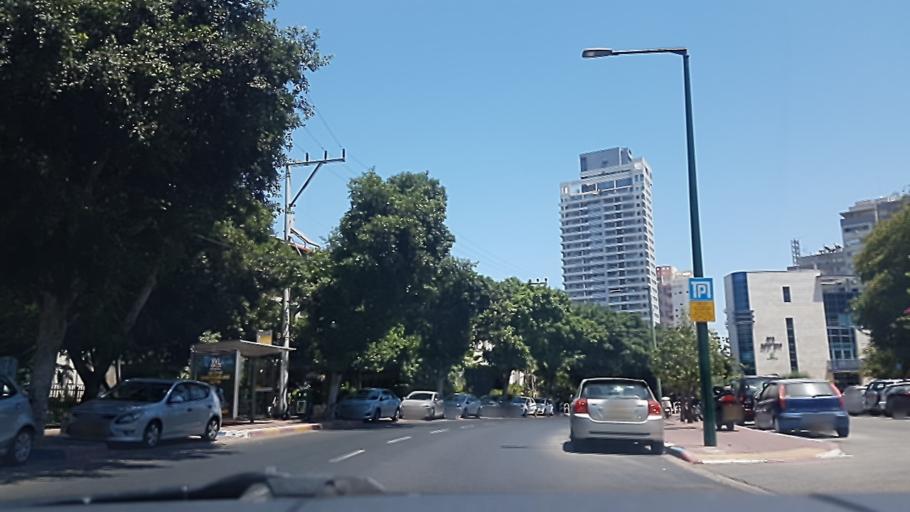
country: IL
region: Tel Aviv
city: Ramat Gan
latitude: 32.0869
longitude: 34.8078
